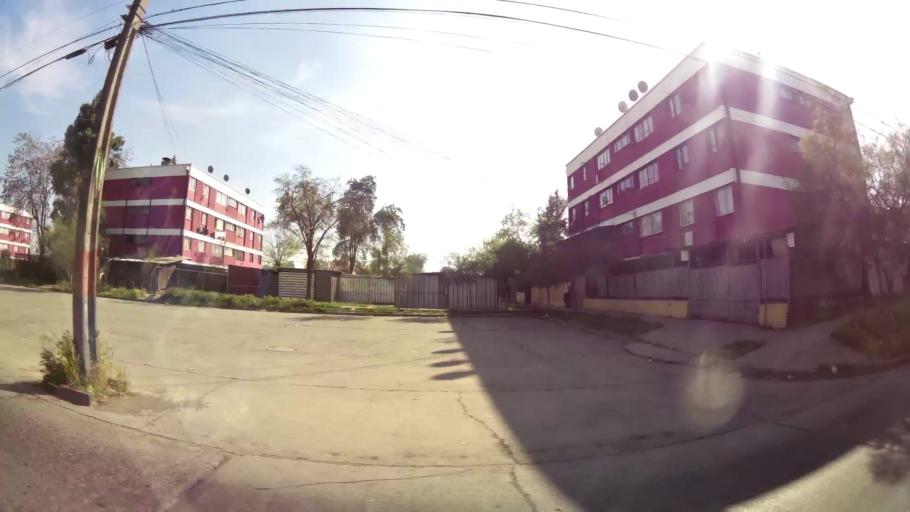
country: CL
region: Santiago Metropolitan
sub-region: Provincia de Santiago
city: Lo Prado
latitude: -33.4518
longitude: -70.7428
